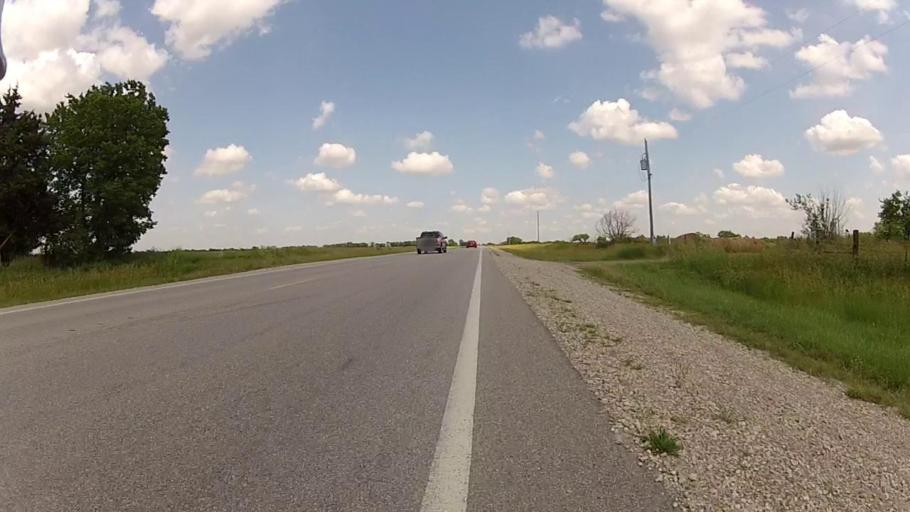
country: US
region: Kansas
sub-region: Labette County
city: Oswego
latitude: 37.1935
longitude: -95.1675
